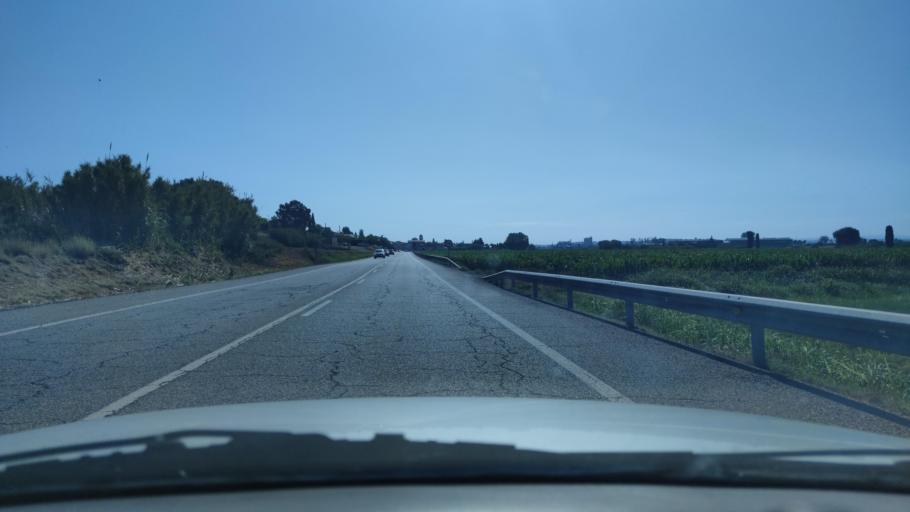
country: ES
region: Catalonia
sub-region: Provincia de Lleida
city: Sidamon
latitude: 41.6285
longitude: 0.7673
